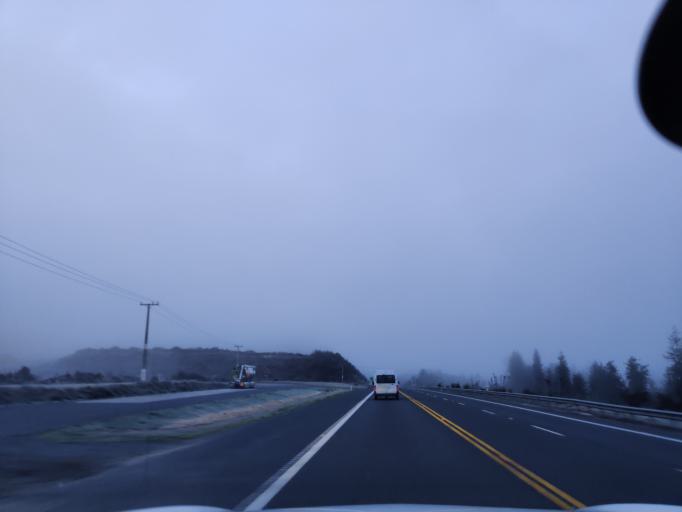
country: NZ
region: Waikato
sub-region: South Waikato District
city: Tokoroa
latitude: -38.3872
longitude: 176.0083
